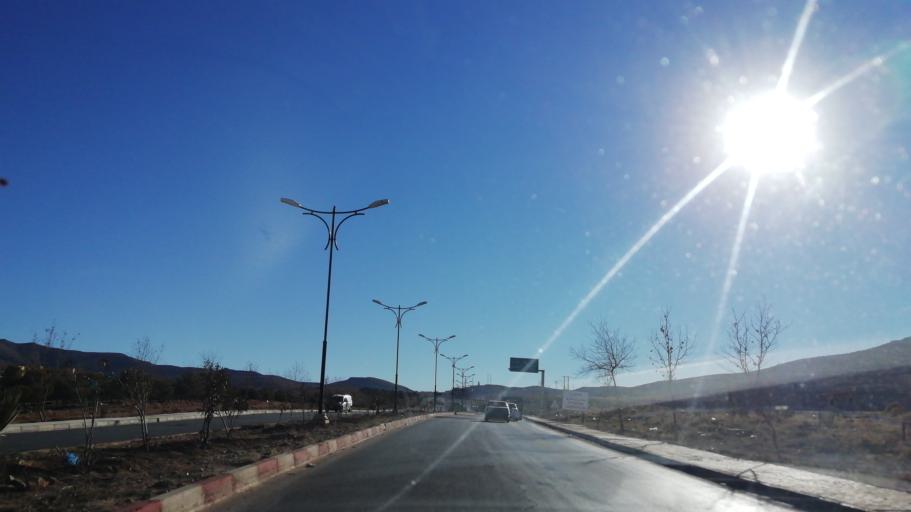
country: DZ
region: El Bayadh
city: El Bayadh
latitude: 33.6582
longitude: 1.0649
